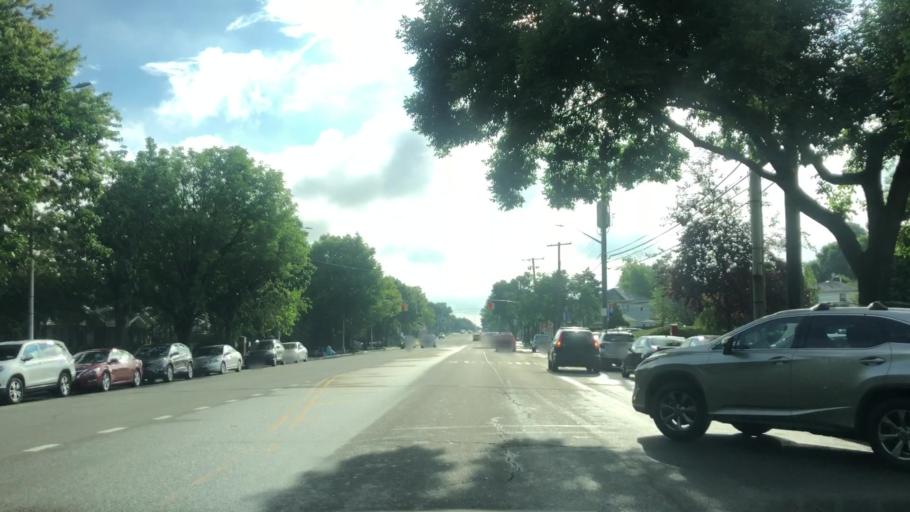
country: US
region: New York
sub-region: Nassau County
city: Bellerose Terrace
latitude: 40.7331
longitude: -73.7280
